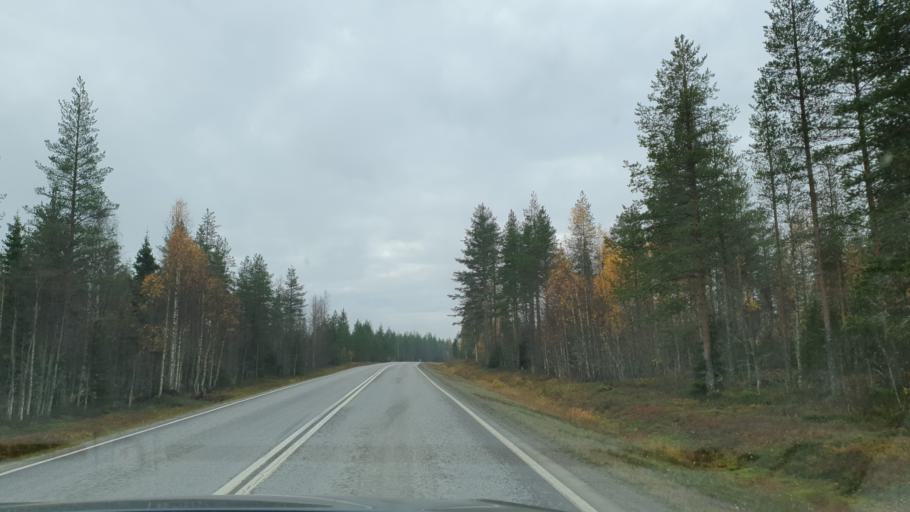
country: FI
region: Lapland
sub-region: Rovaniemi
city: Ranua
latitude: 66.0361
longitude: 26.3363
